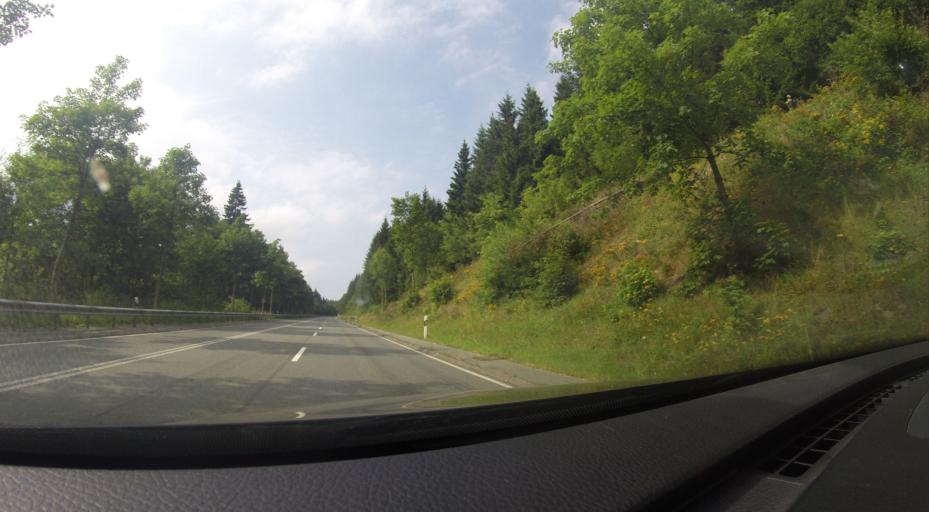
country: DE
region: Hesse
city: Willingen
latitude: 51.2173
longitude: 8.6162
